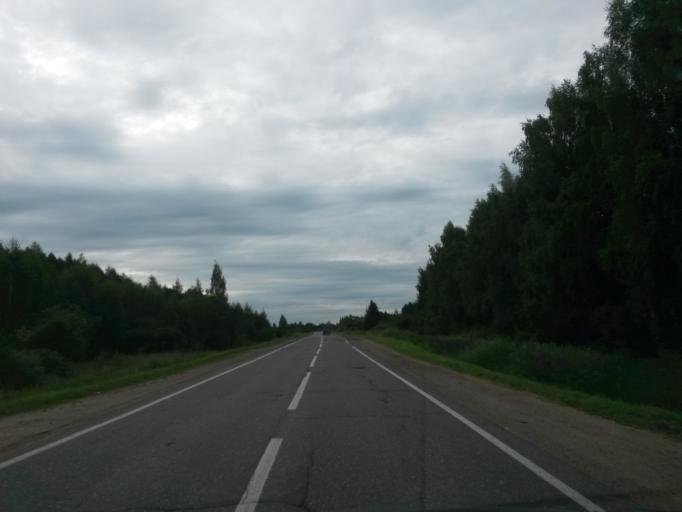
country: RU
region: Jaroslavl
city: Krasnyye Tkachi
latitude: 57.3751
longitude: 39.7238
